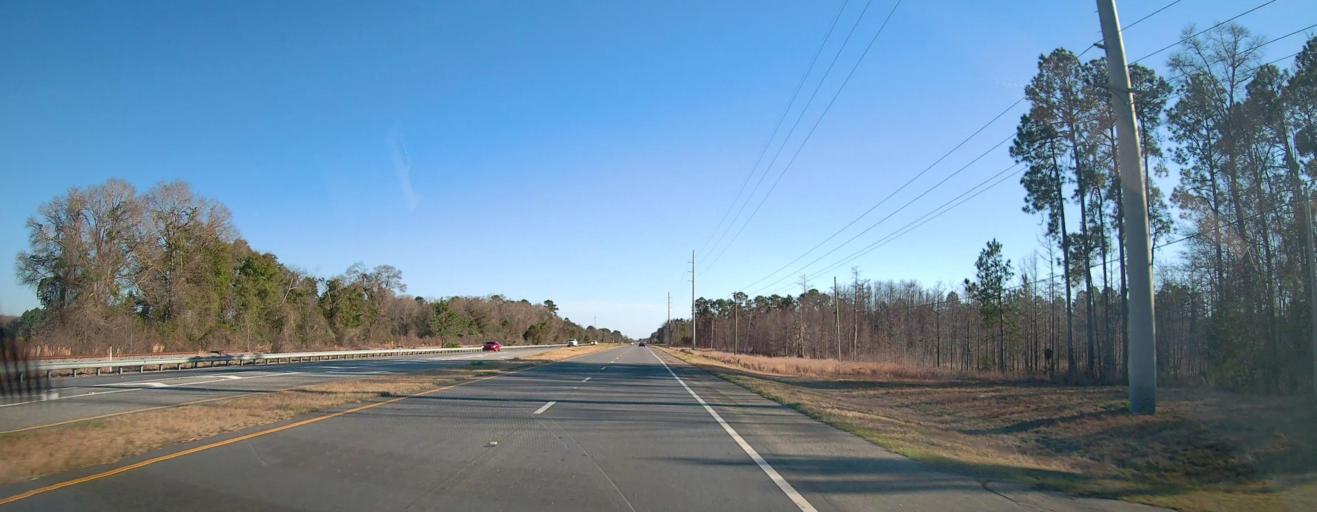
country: US
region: Georgia
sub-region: Lee County
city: Leesburg
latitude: 31.8474
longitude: -84.2269
